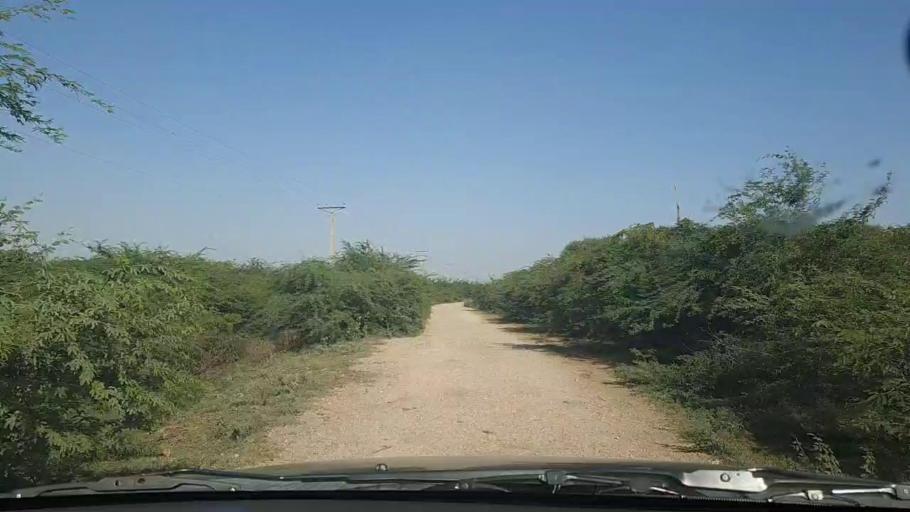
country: PK
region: Sindh
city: Chuhar Jamali
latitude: 24.3238
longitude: 67.7615
